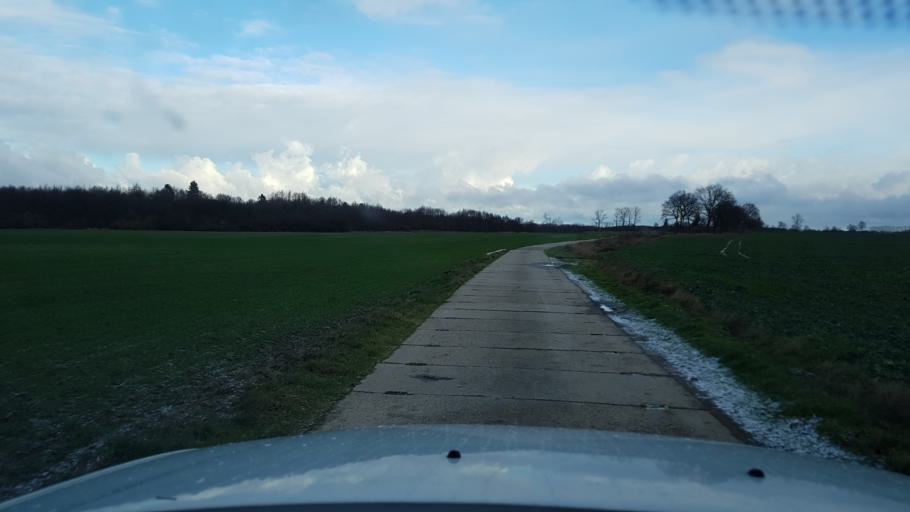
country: PL
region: West Pomeranian Voivodeship
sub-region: Powiat gryficki
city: Brojce
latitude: 54.0408
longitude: 15.3861
